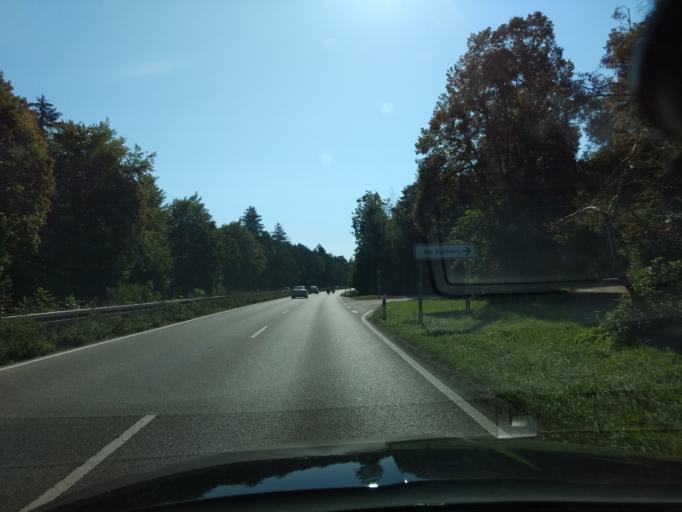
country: DE
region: Bavaria
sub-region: Upper Bavaria
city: Wolfratshausen
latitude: 47.8891
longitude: 11.4494
